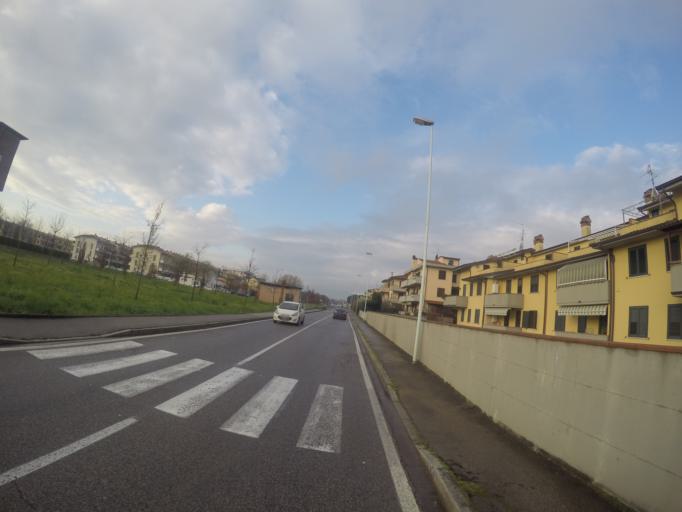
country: IT
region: Tuscany
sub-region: Provincia di Prato
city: Fornacelle
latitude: 43.8912
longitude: 11.0517
